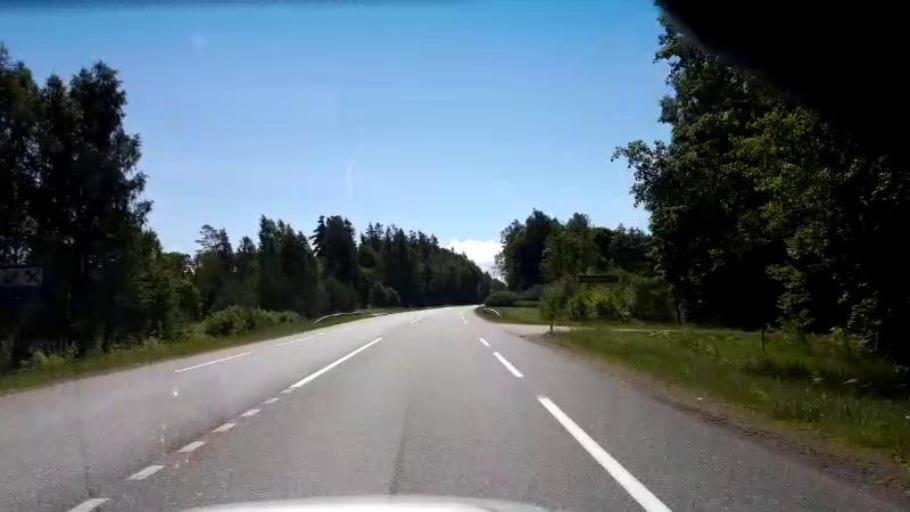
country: LV
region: Saulkrastu
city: Saulkrasti
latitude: 57.3669
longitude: 24.4368
